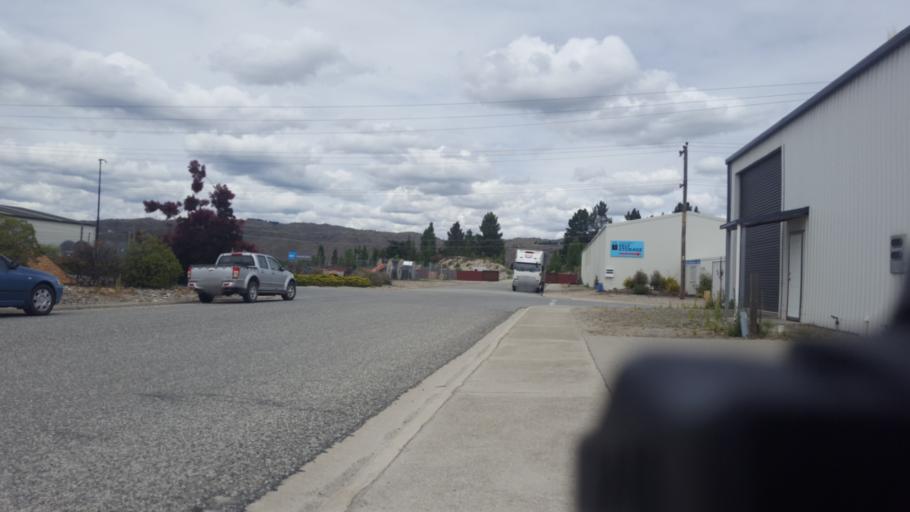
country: NZ
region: Otago
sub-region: Queenstown-Lakes District
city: Wanaka
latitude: -45.2484
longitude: 169.3736
